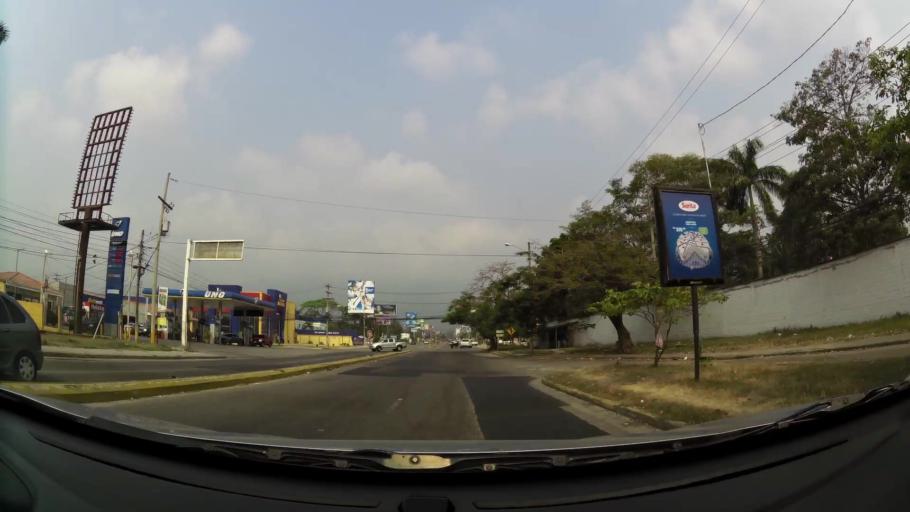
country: HN
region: Cortes
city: San Pedro Sula
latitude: 15.5303
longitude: -88.0226
